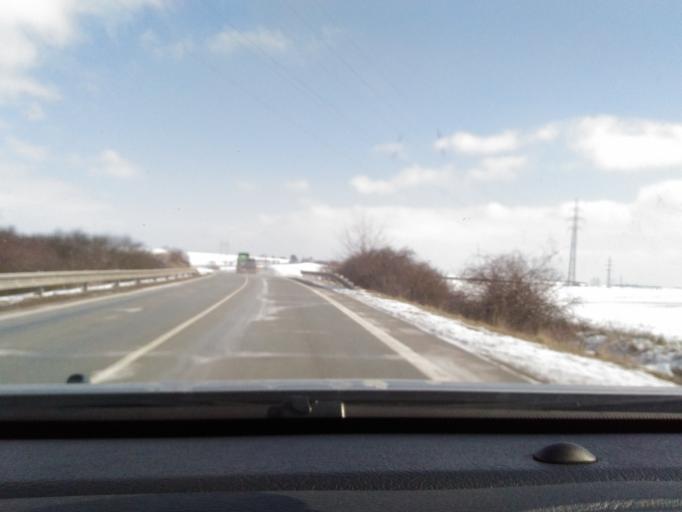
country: CZ
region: Vysocina
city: Krizanov
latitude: 49.3124
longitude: 16.1225
